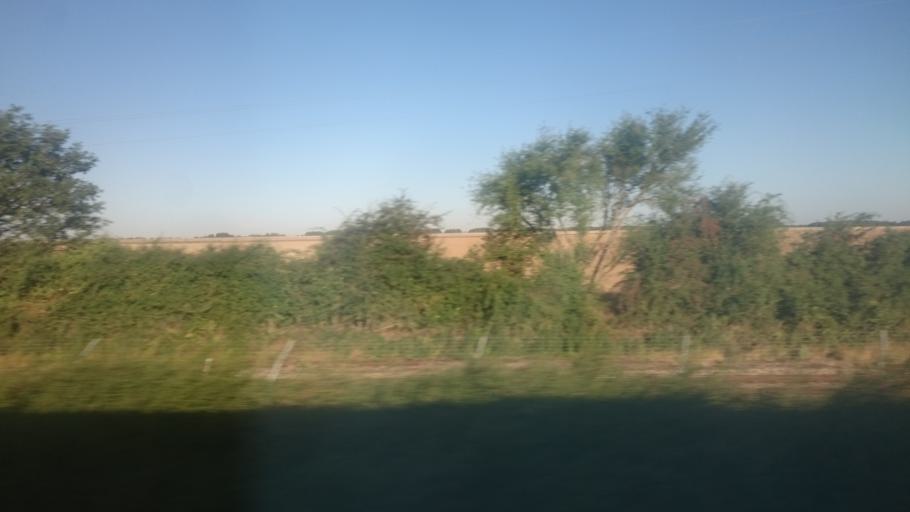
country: FR
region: Centre
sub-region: Departement d'Eure-et-Loir
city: Beville-le-Comte
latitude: 48.3986
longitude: 1.7385
